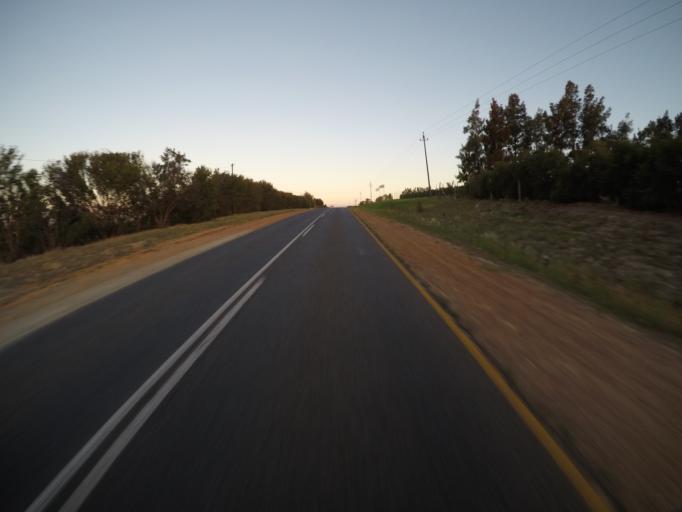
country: ZA
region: Western Cape
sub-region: Cape Winelands District Municipality
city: Paarl
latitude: -33.8090
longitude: 18.9040
